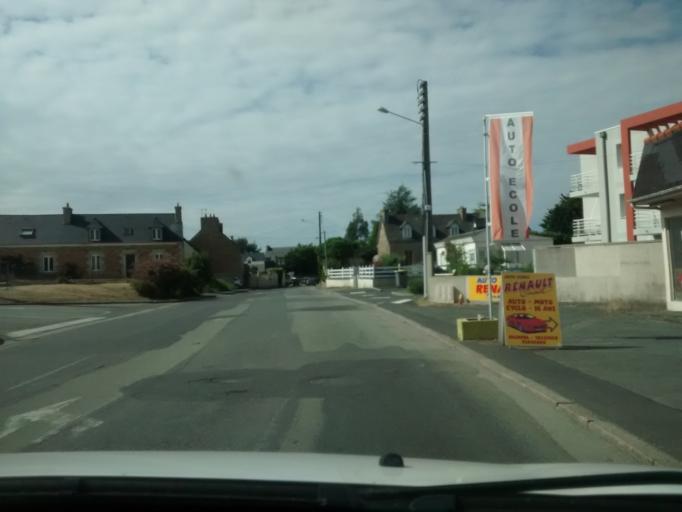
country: FR
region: Brittany
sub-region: Departement des Cotes-d'Armor
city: Penvenan
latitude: 48.8082
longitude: -3.2943
